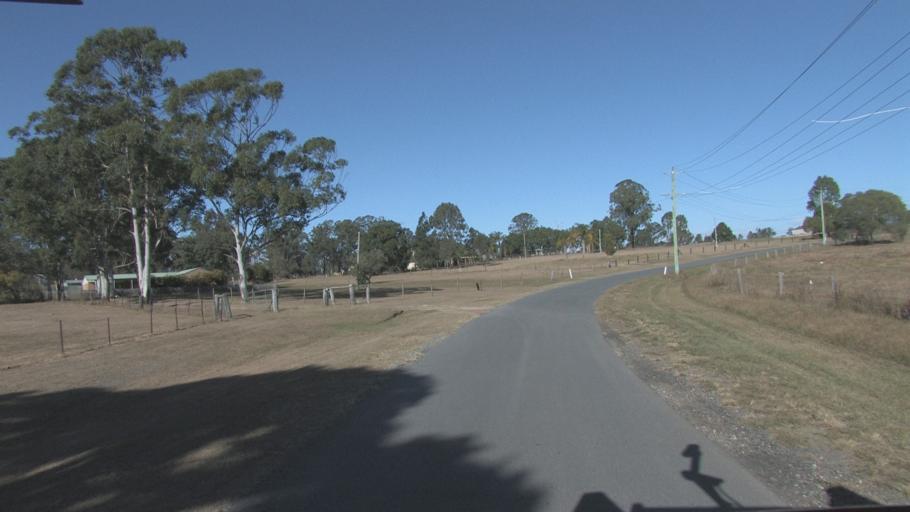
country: AU
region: Queensland
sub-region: Logan
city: Cedar Vale
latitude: -27.8492
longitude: 153.0087
